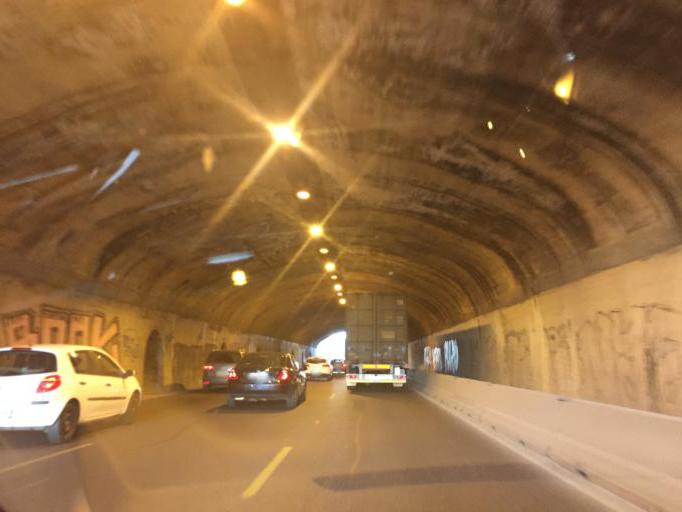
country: FR
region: Provence-Alpes-Cote d'Azur
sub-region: Departement des Bouches-du-Rhone
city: Marseille 15
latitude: 43.3675
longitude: 5.3609
